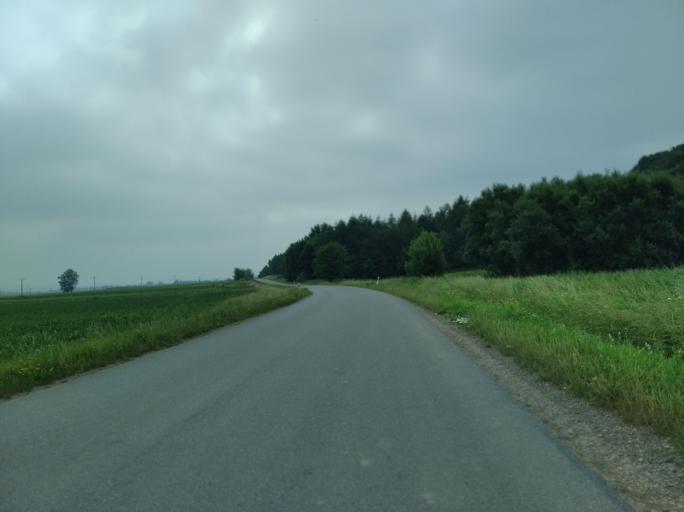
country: PL
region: Subcarpathian Voivodeship
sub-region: Powiat krosnienski
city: Sieniawa
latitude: 49.5973
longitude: 21.9198
